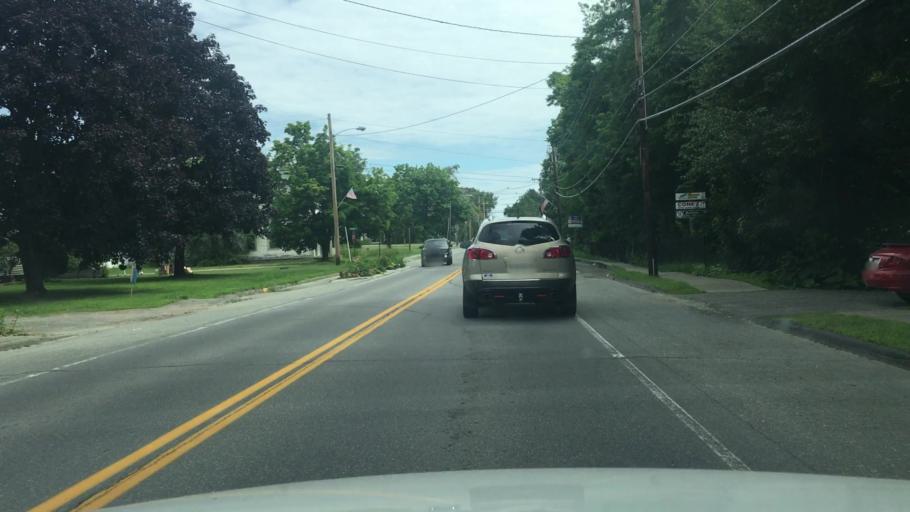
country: US
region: Maine
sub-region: Waldo County
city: Troy
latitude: 44.6123
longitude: -69.3332
